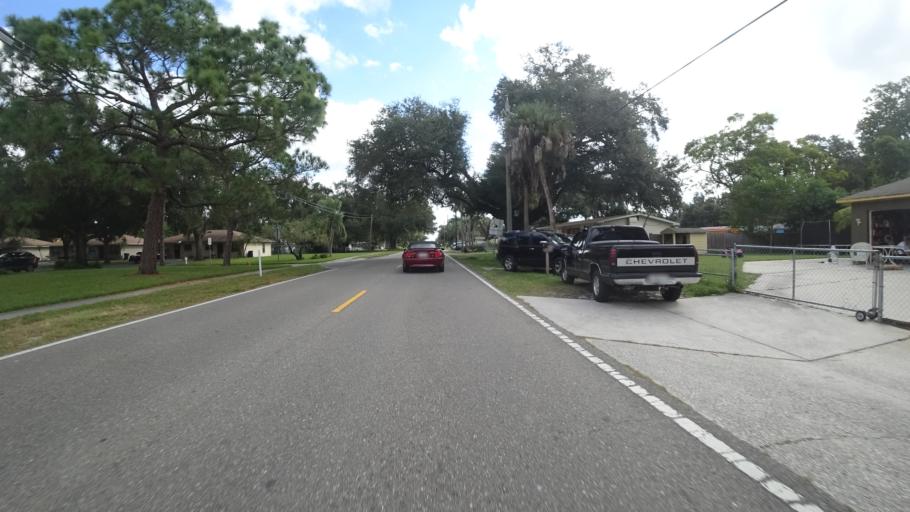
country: US
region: Florida
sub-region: Manatee County
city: Samoset
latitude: 27.4769
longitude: -82.5436
